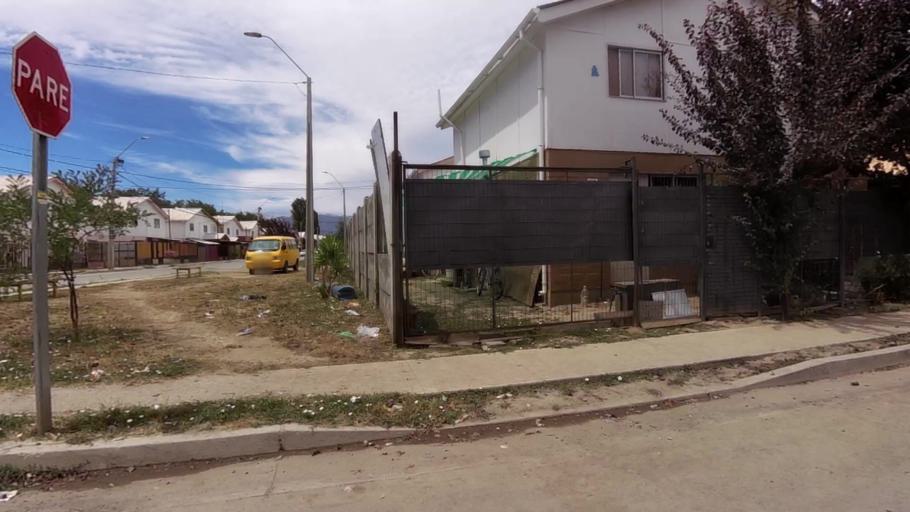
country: CL
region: O'Higgins
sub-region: Provincia de Cachapoal
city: Graneros
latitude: -34.0720
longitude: -70.7404
